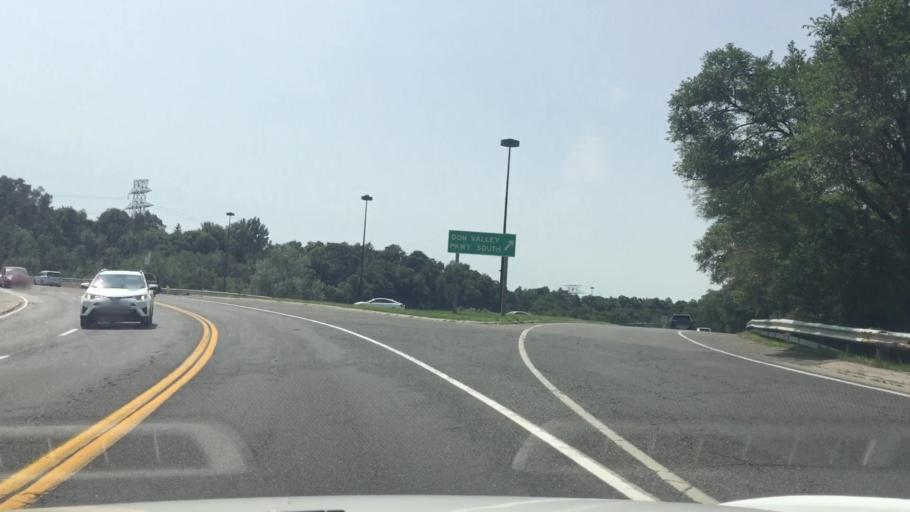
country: CA
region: Ontario
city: Toronto
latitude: 43.7014
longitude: -79.3375
